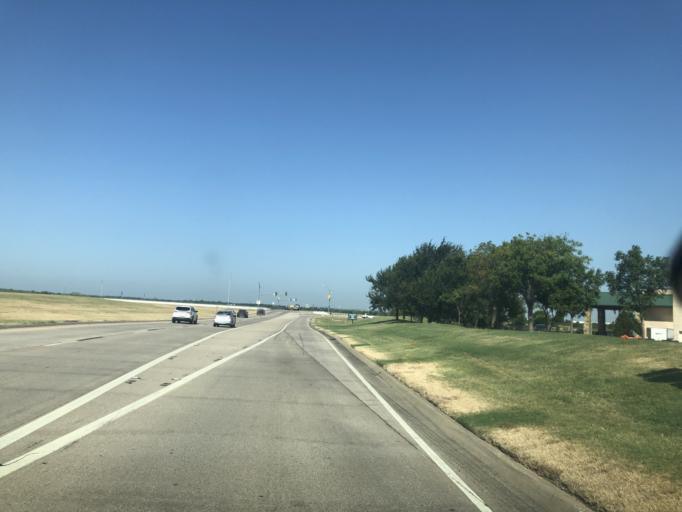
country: US
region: Texas
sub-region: Tarrant County
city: Haslet
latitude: 32.9598
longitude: -97.3076
